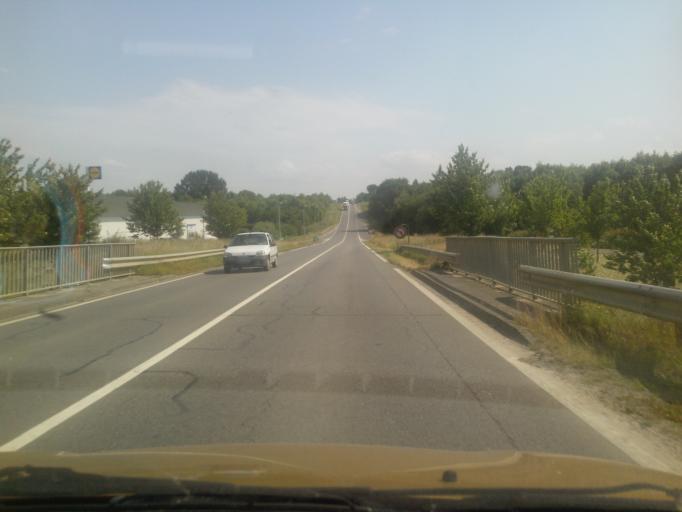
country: FR
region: Brittany
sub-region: Departement d'Ille-et-Vilaine
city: Melesse
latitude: 48.2132
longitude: -1.7009
